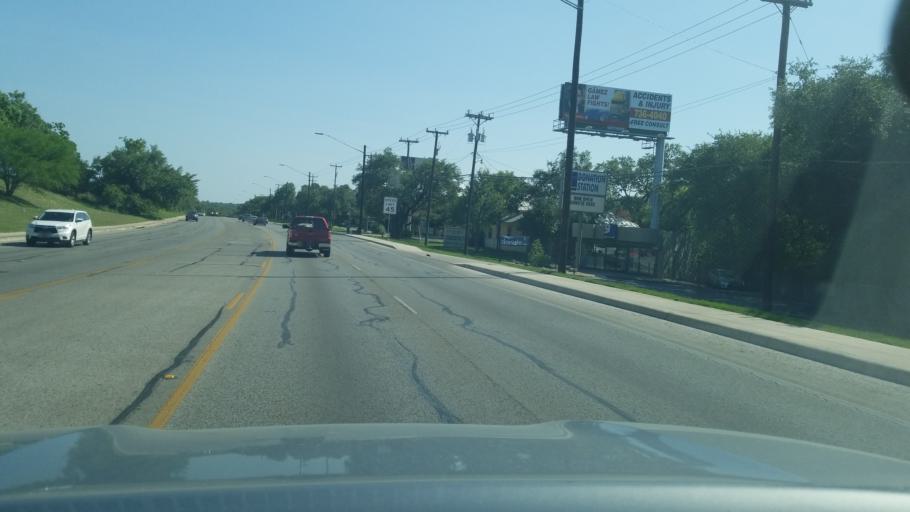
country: US
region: Texas
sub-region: Bexar County
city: Hollywood Park
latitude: 29.5967
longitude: -98.5107
